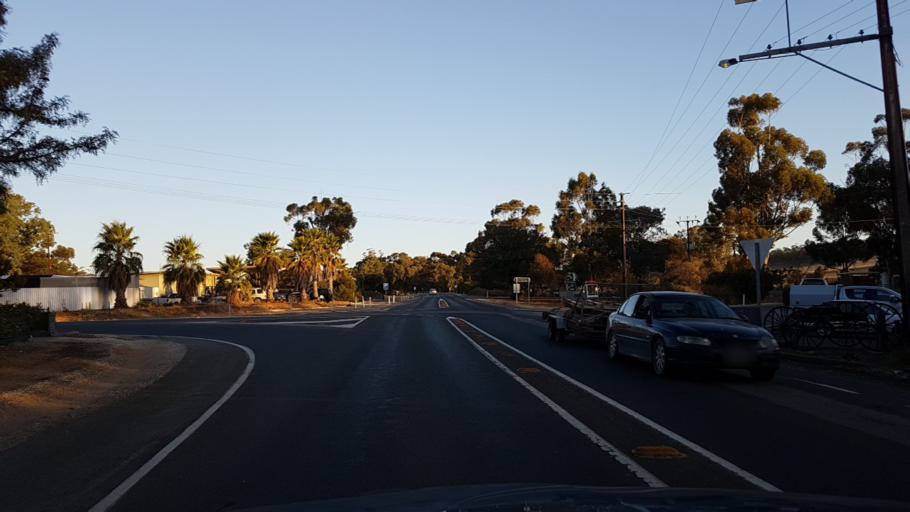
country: AU
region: South Australia
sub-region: Wakefield
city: Balaklava
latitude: -34.1476
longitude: 138.6898
